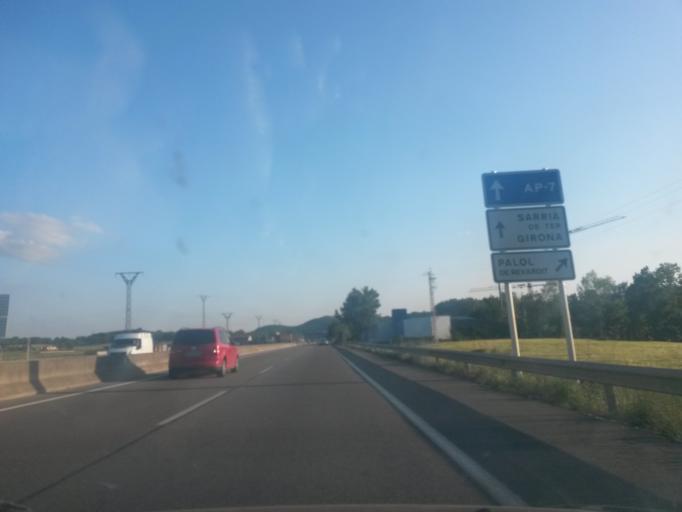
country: ES
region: Catalonia
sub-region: Provincia de Girona
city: Cornella del Terri
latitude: 42.0786
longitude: 2.8177
